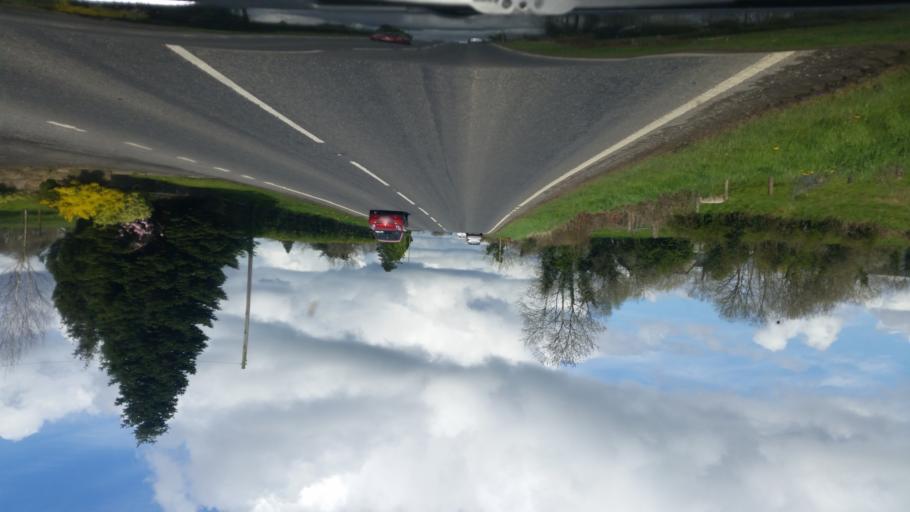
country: IE
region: Ulster
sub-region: An Cabhan
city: Ballyconnell
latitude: 54.1463
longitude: -7.5173
